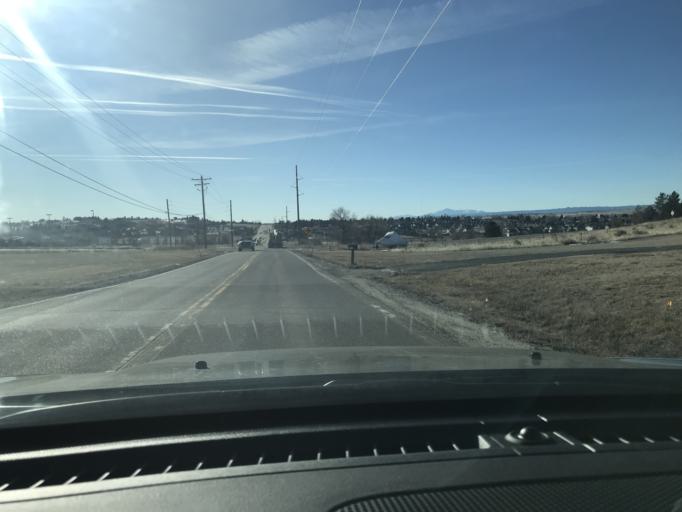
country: US
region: Colorado
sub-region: Douglas County
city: Parker
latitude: 39.5404
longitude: -104.7559
